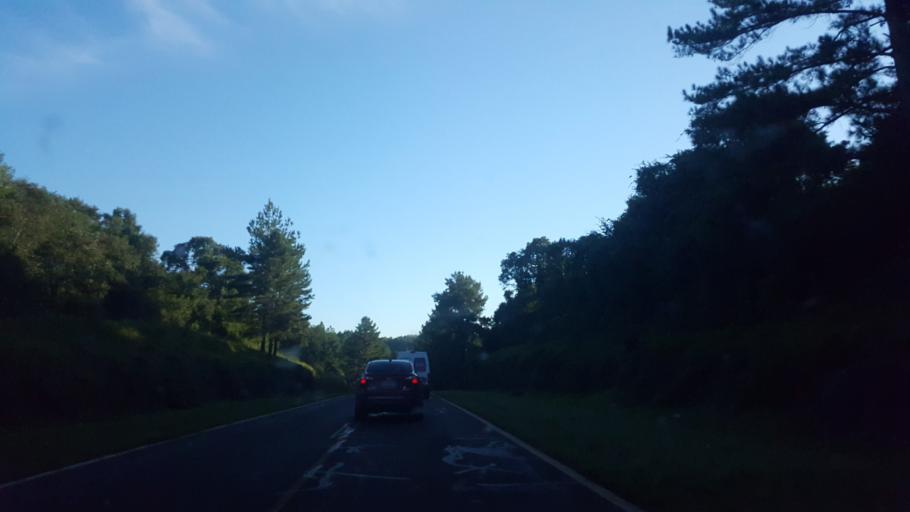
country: AR
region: Misiones
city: El Alcazar
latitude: -26.7593
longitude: -54.8864
